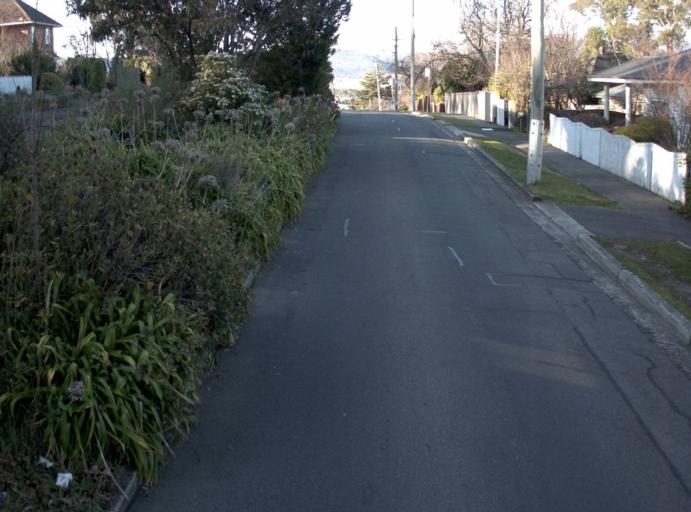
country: AU
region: Tasmania
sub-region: Launceston
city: Summerhill
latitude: -41.4639
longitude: 147.1514
